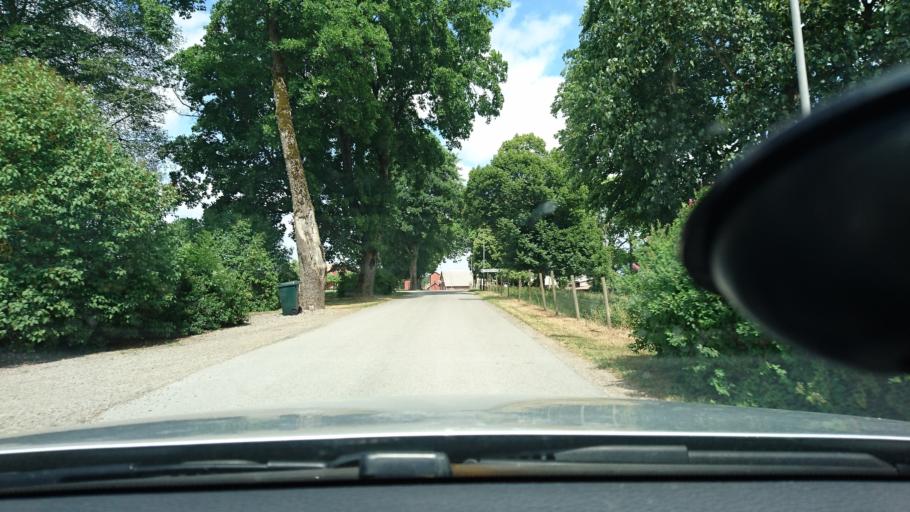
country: SE
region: Kronoberg
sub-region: Alvesta Kommun
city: Moheda
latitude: 56.9491
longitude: 14.5713
